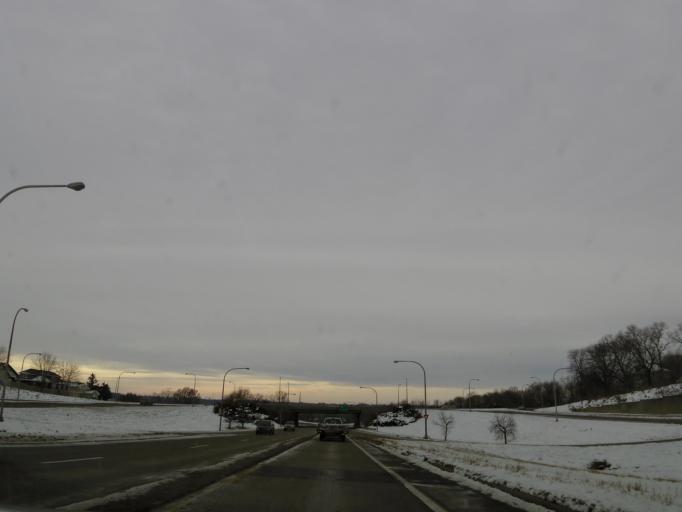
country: US
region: Illinois
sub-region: LaSalle County
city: Peru
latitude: 41.3291
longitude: -89.1200
